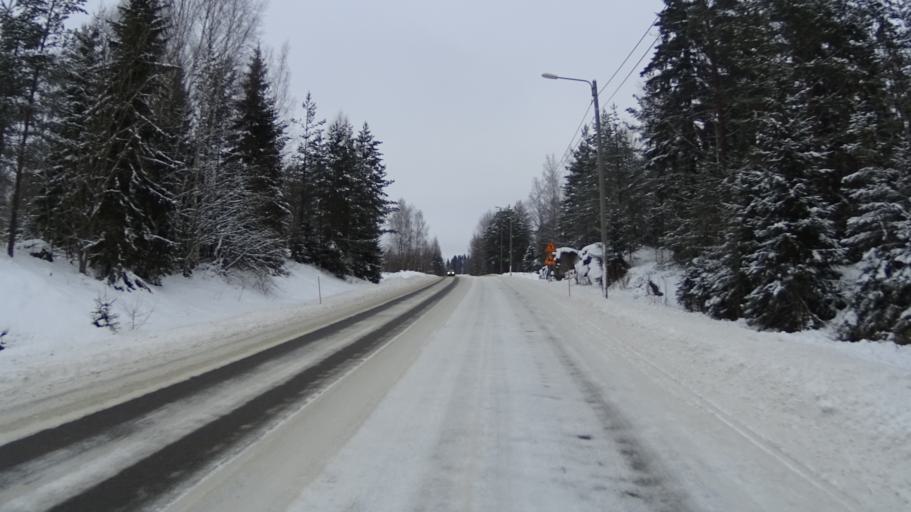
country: FI
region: Uusimaa
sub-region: Helsinki
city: Karkkila
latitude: 60.5227
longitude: 24.2022
